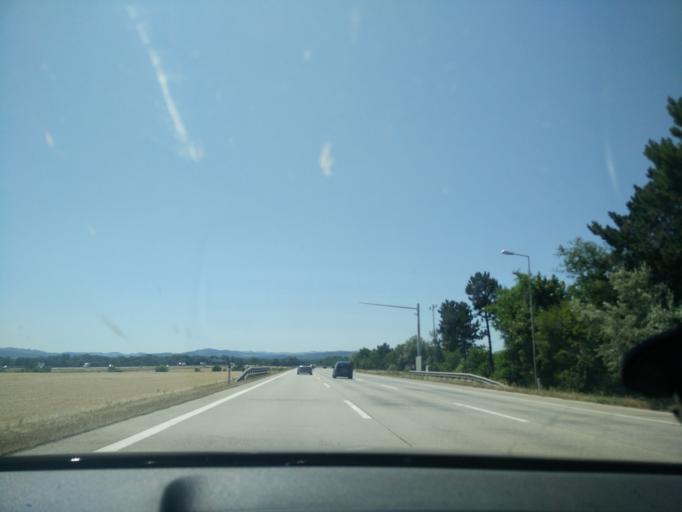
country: AT
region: Lower Austria
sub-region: Wiener Neustadt Stadt
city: Wiener Neustadt
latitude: 47.7808
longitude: 16.2040
